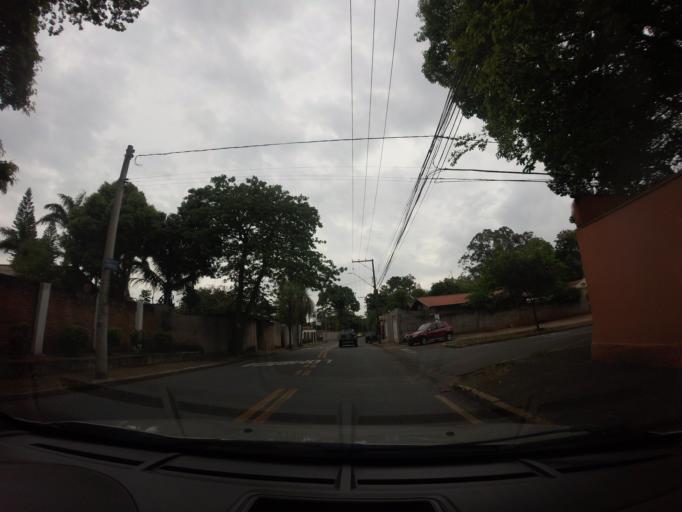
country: BR
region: Sao Paulo
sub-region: Piracicaba
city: Piracicaba
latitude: -22.7421
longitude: -47.5970
